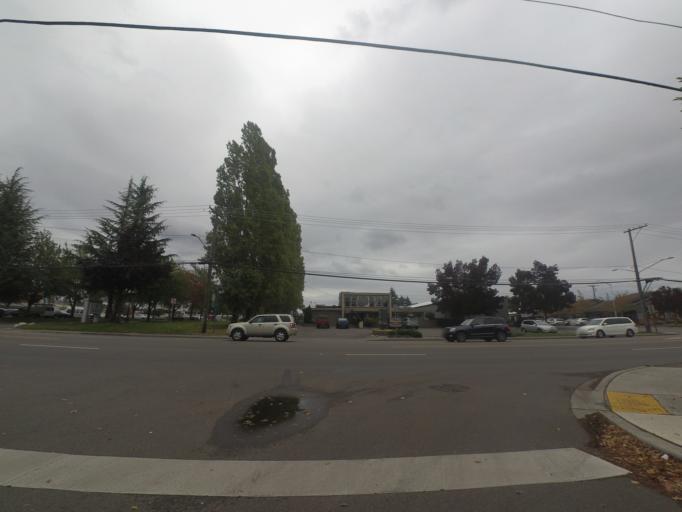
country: US
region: Washington
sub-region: Pierce County
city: Lakewood
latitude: 47.1535
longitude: -122.5047
